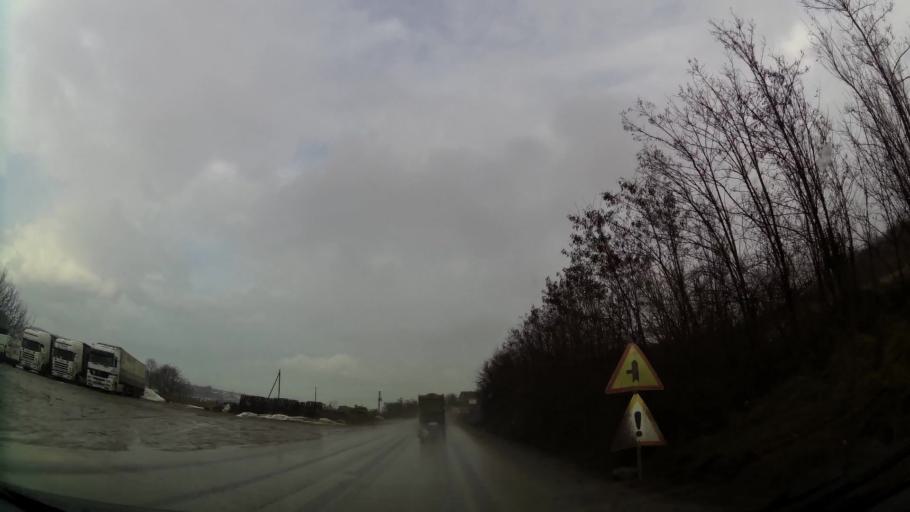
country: XK
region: Ferizaj
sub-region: Komuna e Kacanikut
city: Kacanik
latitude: 42.2446
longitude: 21.2410
